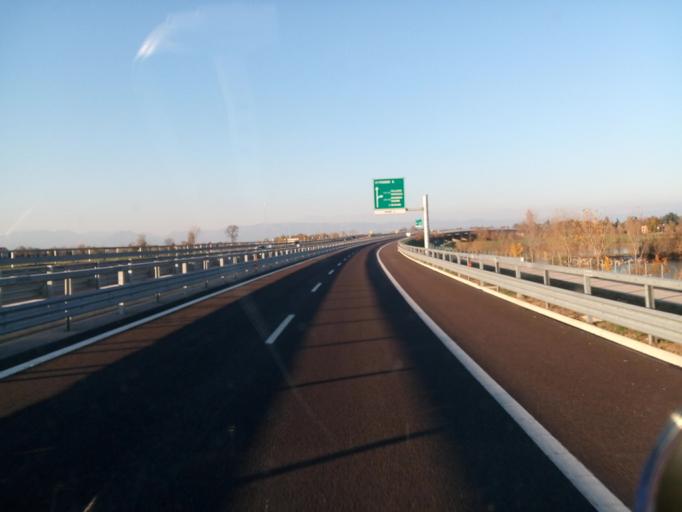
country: IT
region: Veneto
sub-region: Provincia di Vicenza
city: Torri di Quartesolo
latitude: 45.4986
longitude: 11.6163
